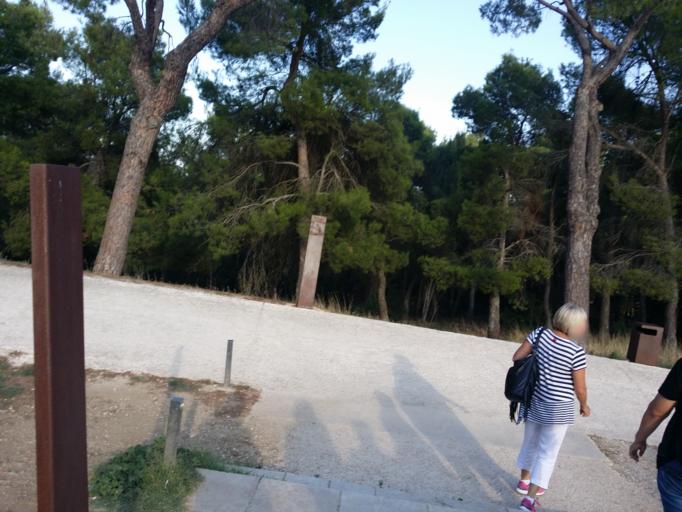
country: IT
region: Apulia
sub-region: Provincia di Bari
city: Corato
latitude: 41.0846
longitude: 16.2719
